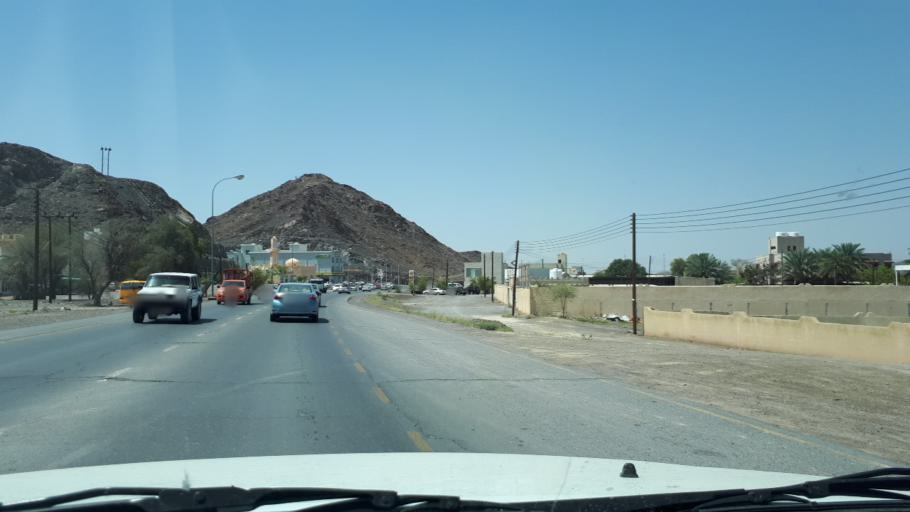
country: OM
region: Muhafazat ad Dakhiliyah
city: Bahla'
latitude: 22.9814
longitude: 57.3085
